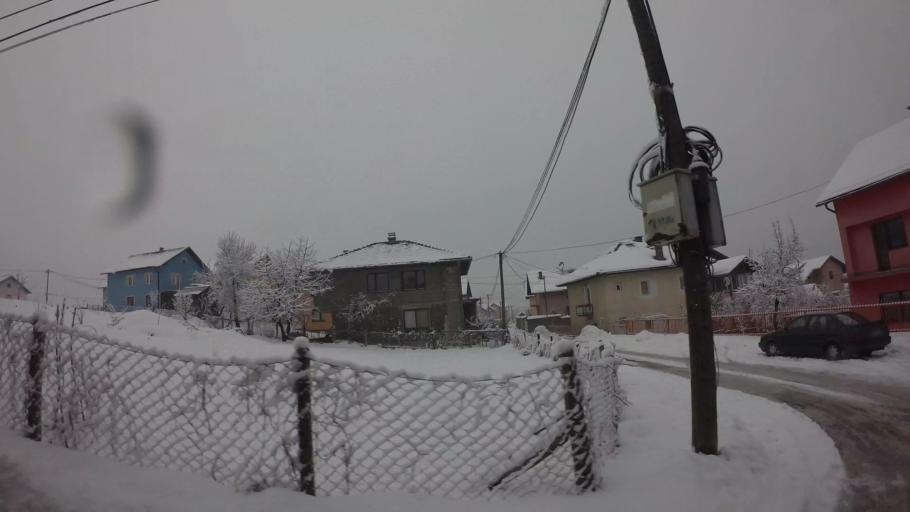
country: BA
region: Federation of Bosnia and Herzegovina
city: Vogosca
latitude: 43.8707
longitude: 18.3186
